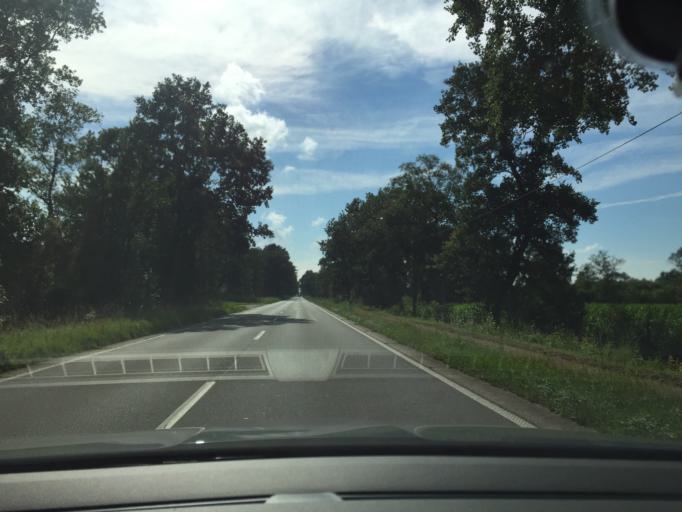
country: DE
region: Lower Saxony
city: Dunum
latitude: 53.5499
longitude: 7.6470
